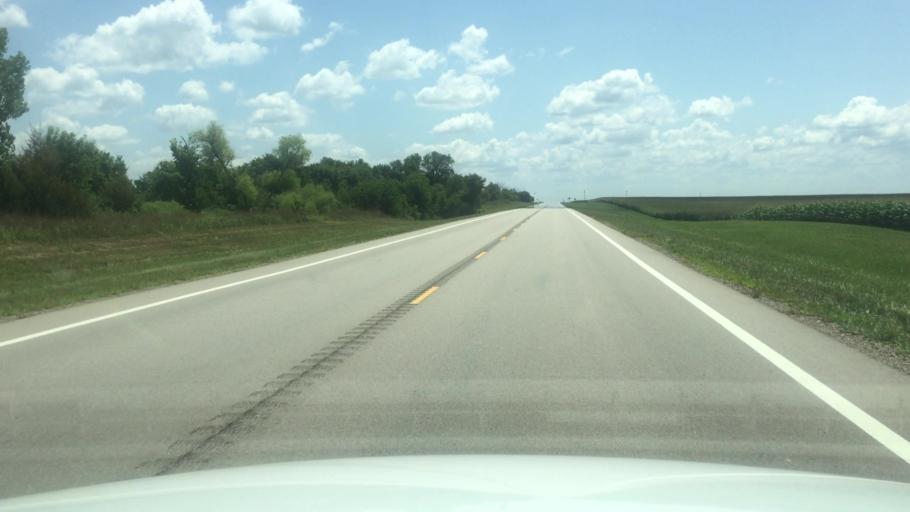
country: US
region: Kansas
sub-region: Brown County
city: Horton
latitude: 39.6446
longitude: -95.3549
